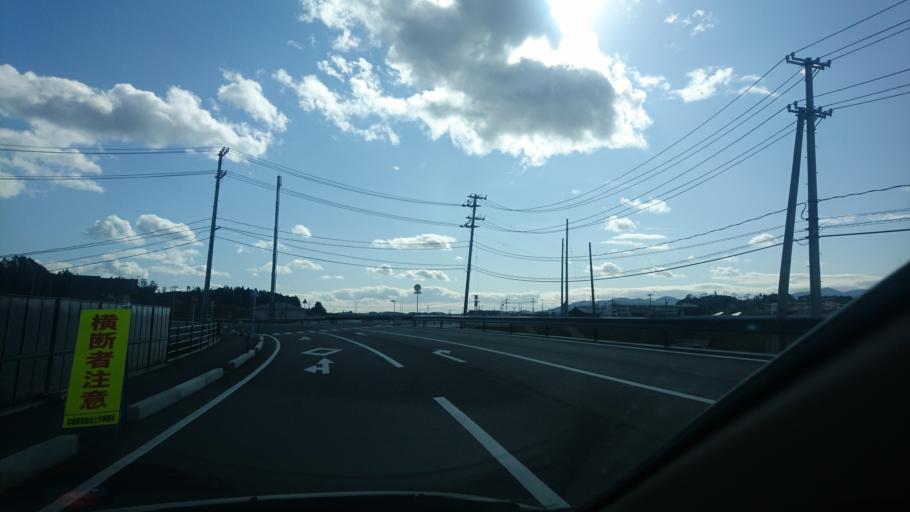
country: JP
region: Iwate
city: Ofunato
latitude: 38.9186
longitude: 141.5868
